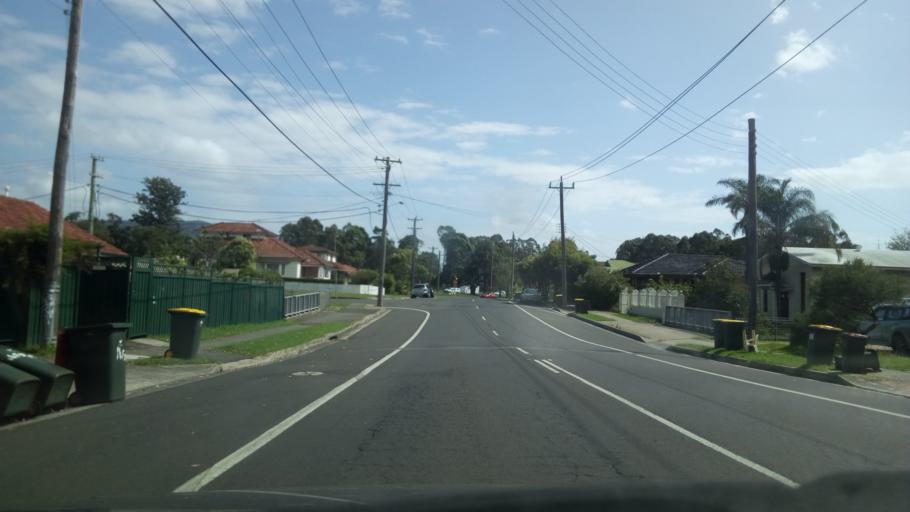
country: AU
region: New South Wales
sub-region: Wollongong
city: Gwynneville
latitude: -34.4136
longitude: 150.8857
